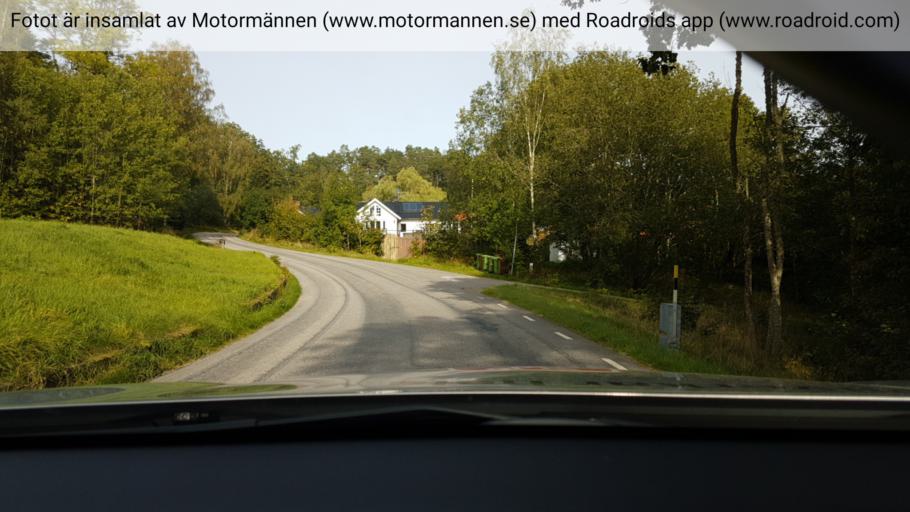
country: SE
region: Vaestra Goetaland
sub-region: Uddevalla Kommun
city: Ljungskile
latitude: 58.2300
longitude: 11.9048
